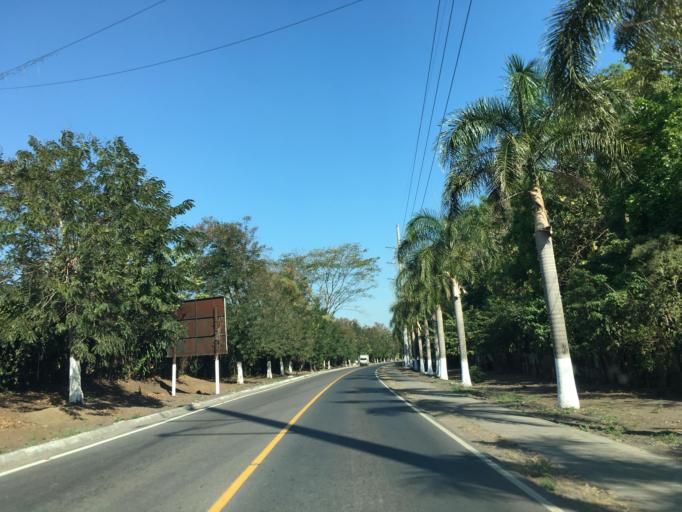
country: GT
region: Escuintla
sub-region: Municipio de La Democracia
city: La Democracia
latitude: 14.2375
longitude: -90.9539
